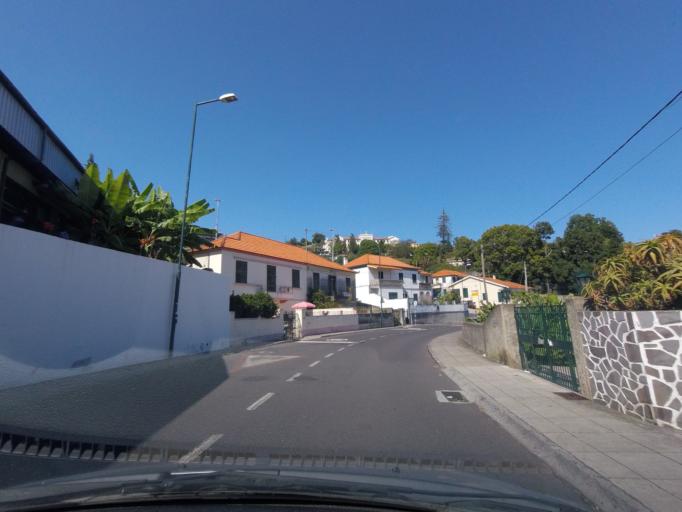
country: PT
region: Madeira
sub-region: Funchal
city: Nossa Senhora do Monte
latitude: 32.6586
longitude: -16.9096
